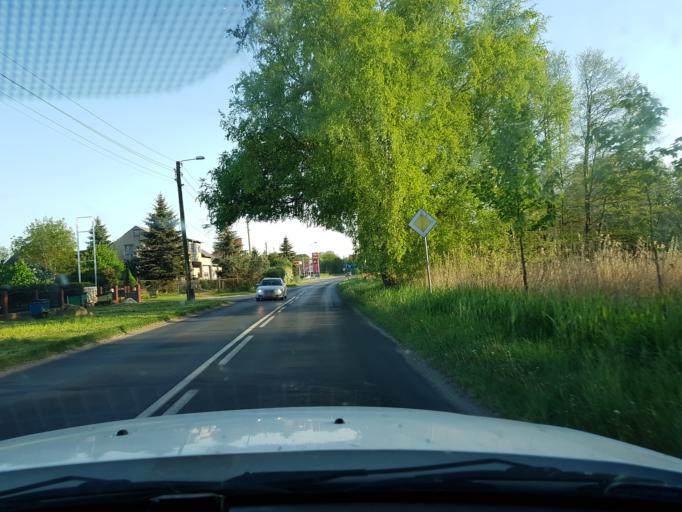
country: PL
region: West Pomeranian Voivodeship
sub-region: Powiat goleniowski
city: Maszewo
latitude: 53.4953
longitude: 15.0660
